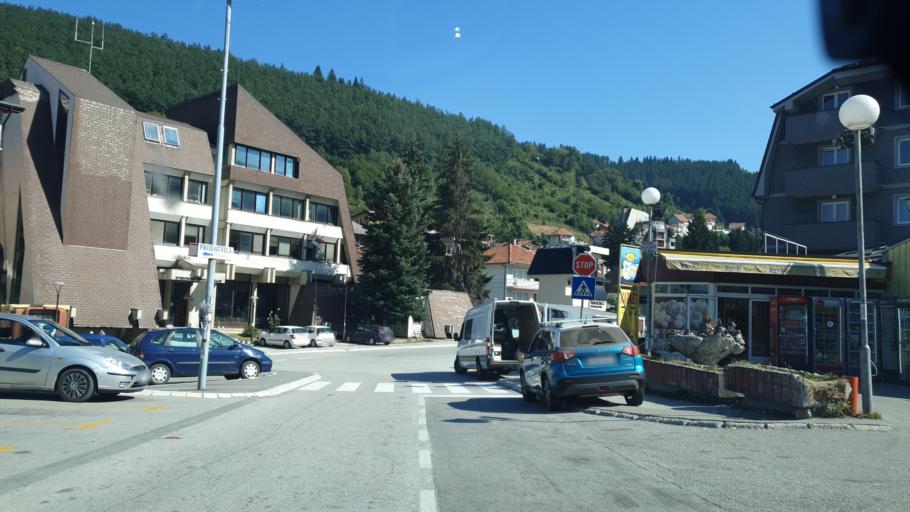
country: RS
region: Central Serbia
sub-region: Zlatiborski Okrug
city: Nova Varos
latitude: 43.4594
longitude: 19.8128
